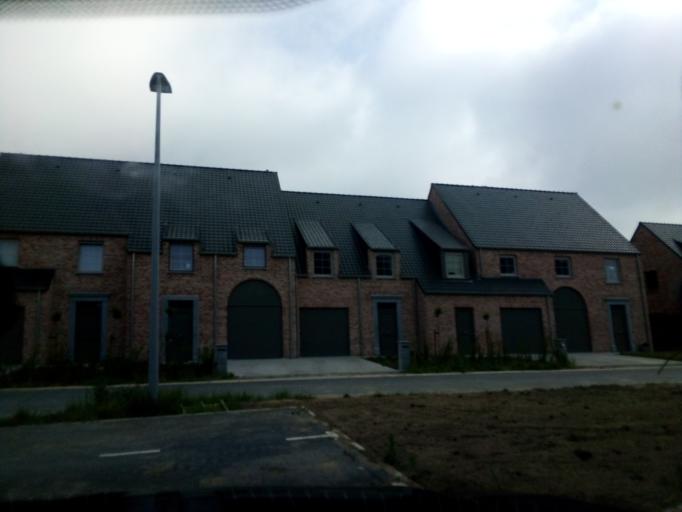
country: BE
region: Flanders
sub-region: Provincie West-Vlaanderen
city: Ingelmunster
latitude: 50.9261
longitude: 3.2500
